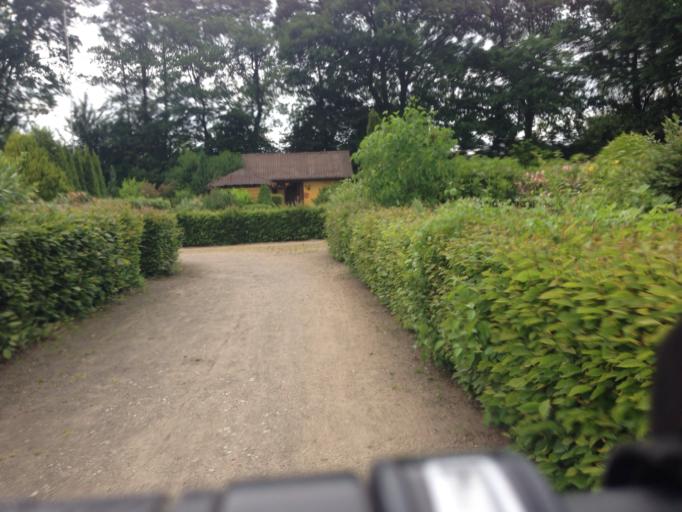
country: DE
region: Schleswig-Holstein
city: Barsbuettel
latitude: 53.5857
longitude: 10.1771
